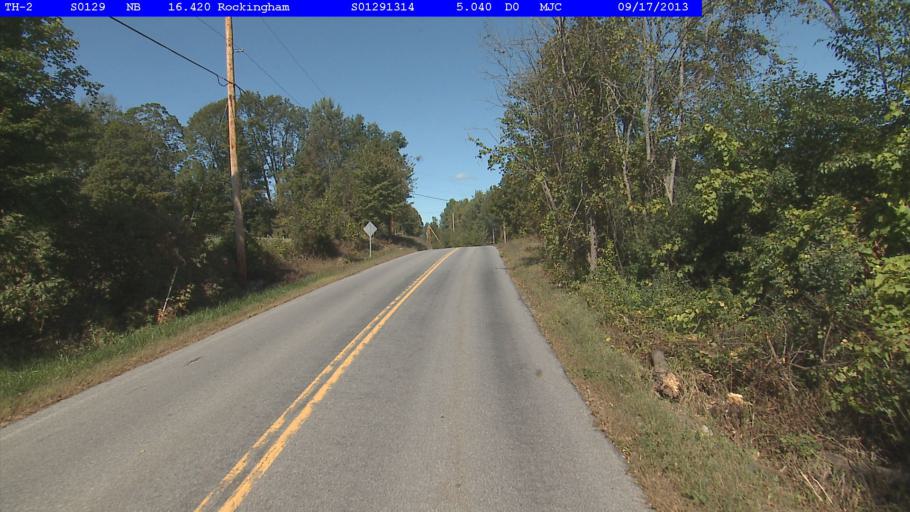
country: US
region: Vermont
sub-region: Windham County
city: Rockingham
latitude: 43.1890
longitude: -72.5117
